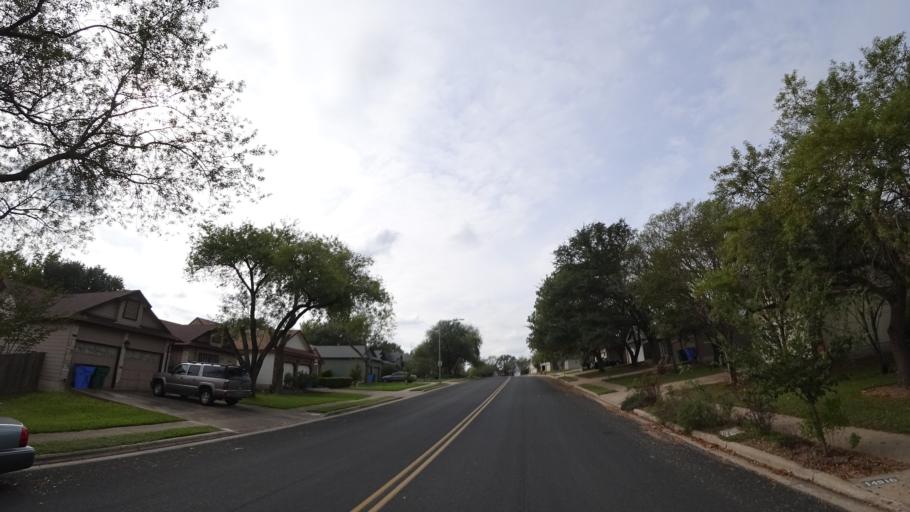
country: US
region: Texas
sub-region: Travis County
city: Wells Branch
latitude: 30.4460
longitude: -97.6766
